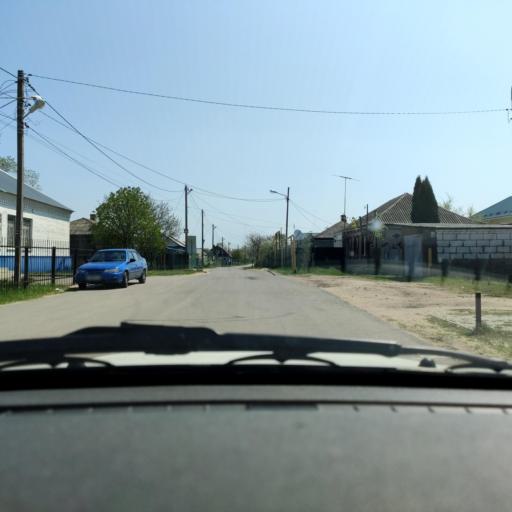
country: RU
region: Voronezj
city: Shilovo
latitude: 51.5584
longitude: 39.0639
